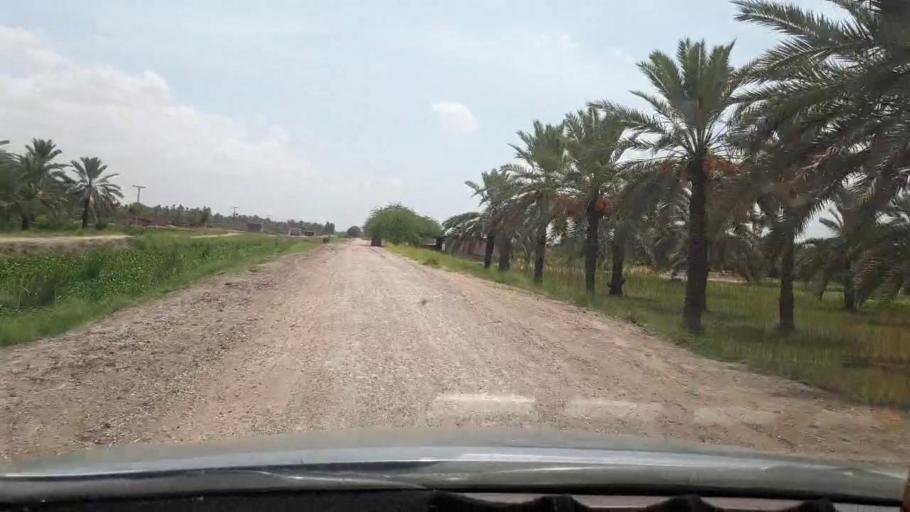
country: PK
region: Sindh
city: Khairpur
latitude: 27.4565
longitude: 68.7901
